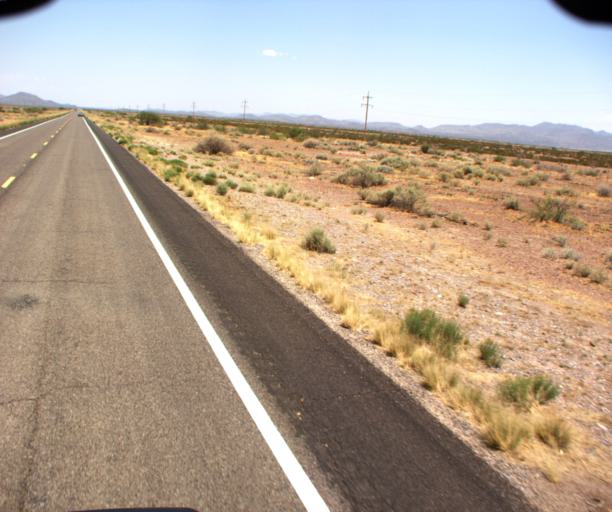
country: US
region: Arizona
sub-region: Graham County
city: Safford
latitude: 32.7765
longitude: -109.5090
